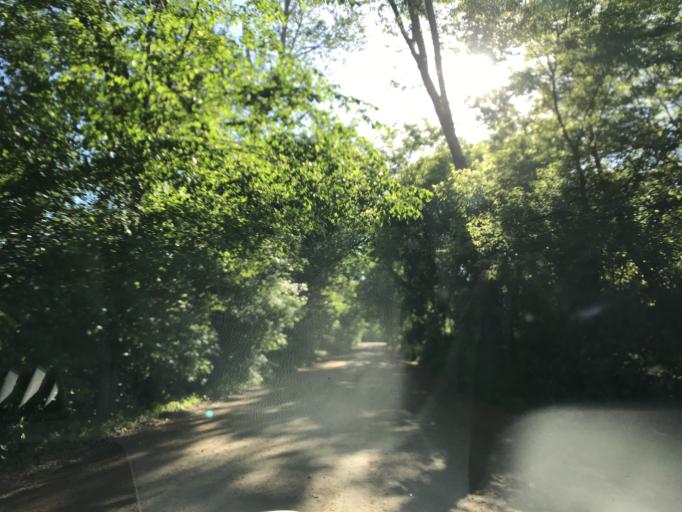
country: US
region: Michigan
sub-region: Oakland County
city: South Lyon
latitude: 42.4973
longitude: -83.6366
